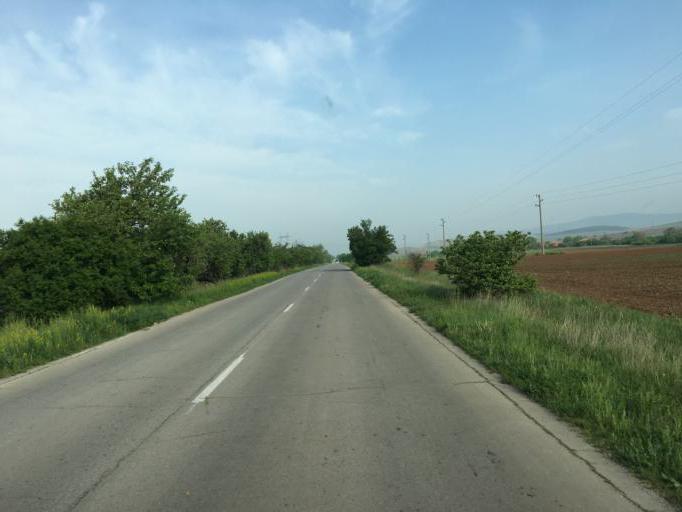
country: BG
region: Pernik
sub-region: Obshtina Radomir
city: Radomir
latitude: 42.4828
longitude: 23.0561
